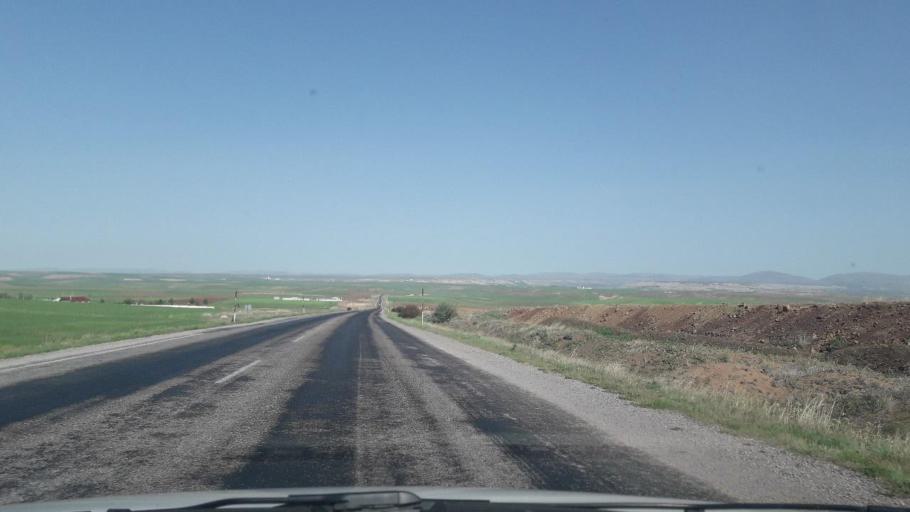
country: TR
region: Sivas
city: Kangal
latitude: 39.1733
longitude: 37.4551
